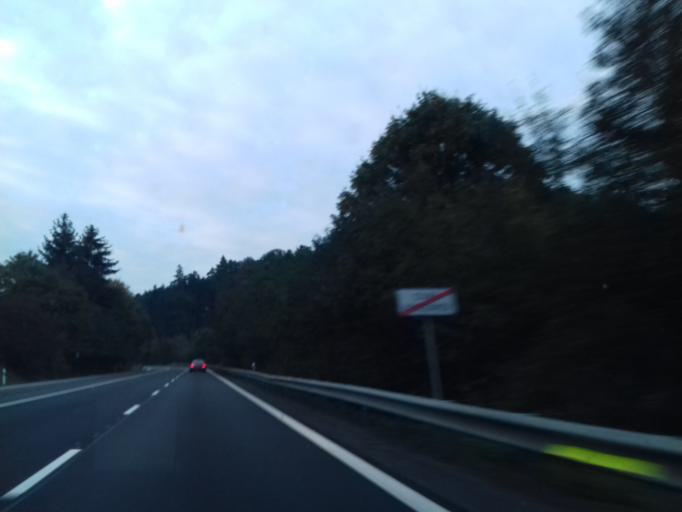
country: CZ
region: Zlin
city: Bojkovice
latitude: 48.9722
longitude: 17.8607
